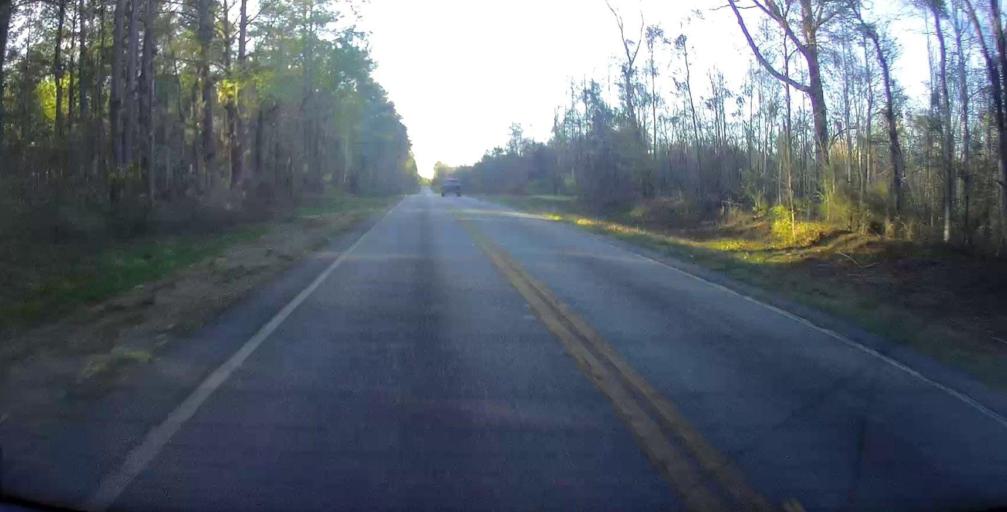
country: US
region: Georgia
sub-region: Wilcox County
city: Abbeville
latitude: 32.1057
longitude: -83.3102
